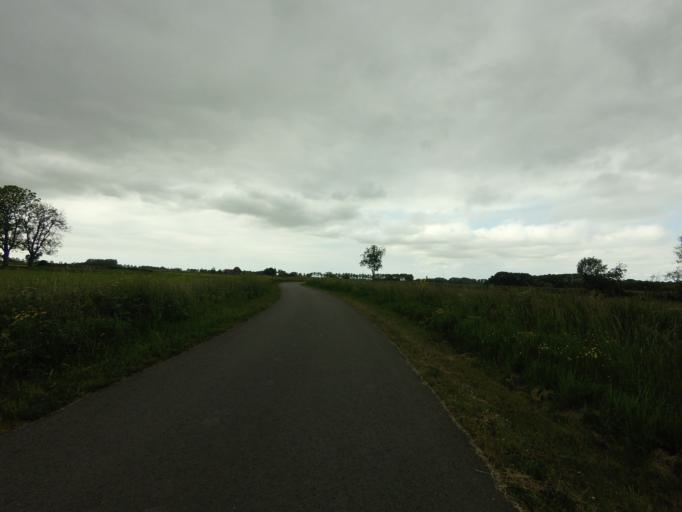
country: NL
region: North Holland
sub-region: Gemeente Hoorn
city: Hoorn
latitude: 52.6662
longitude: 5.0173
